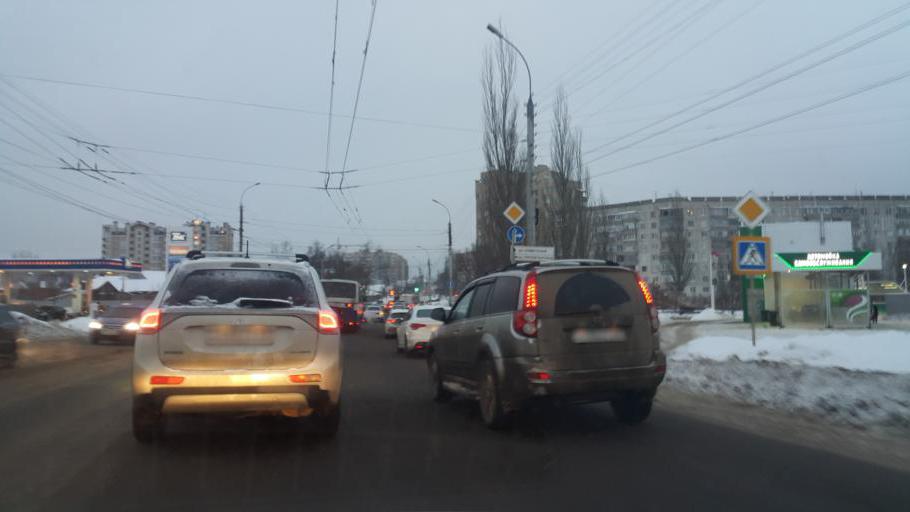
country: RU
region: Tambov
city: Tambov
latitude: 52.6995
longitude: 41.4627
